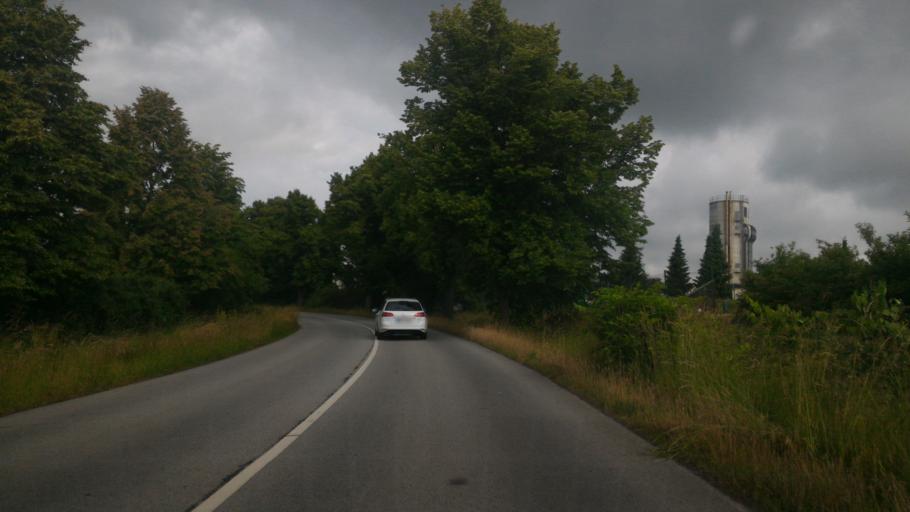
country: DE
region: Saxony
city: Neugersdorf
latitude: 50.9803
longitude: 14.6261
